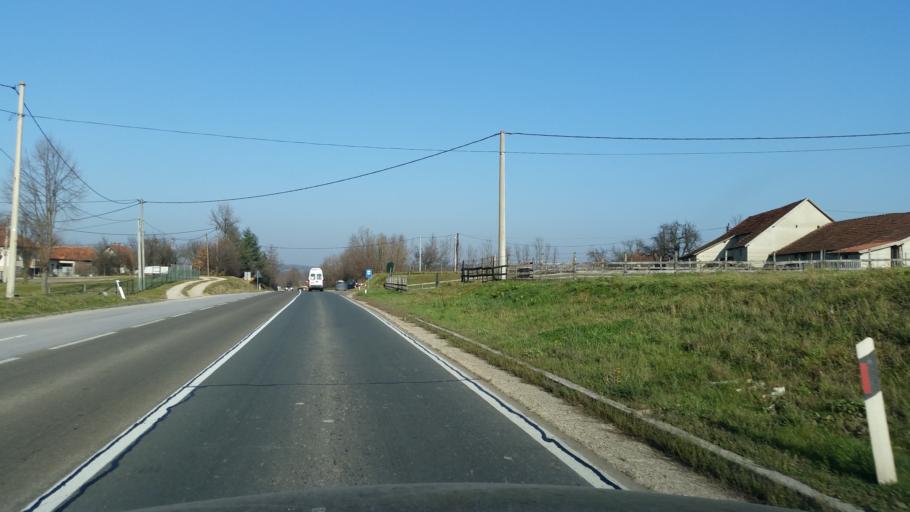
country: RS
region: Central Serbia
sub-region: Kolubarski Okrug
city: Ljig
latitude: 44.2498
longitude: 20.2846
